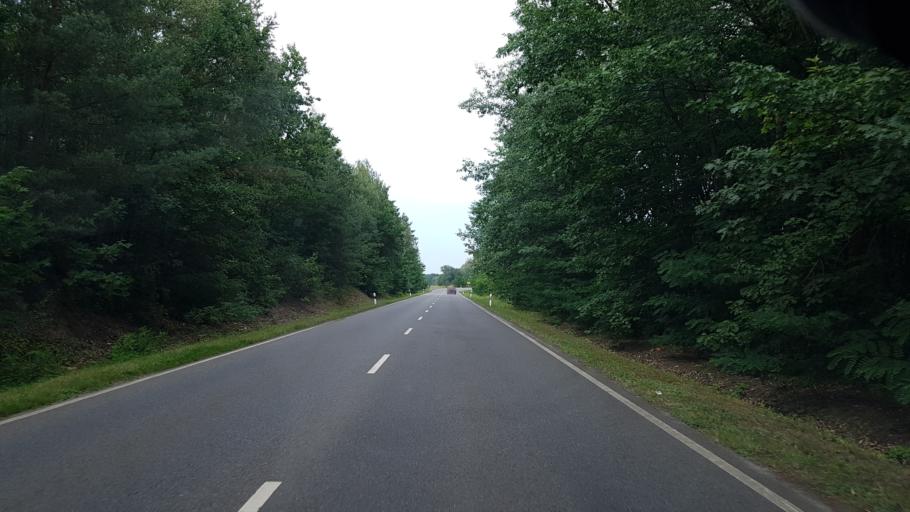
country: DE
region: Brandenburg
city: Lauchhammer
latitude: 51.5045
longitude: 13.7437
